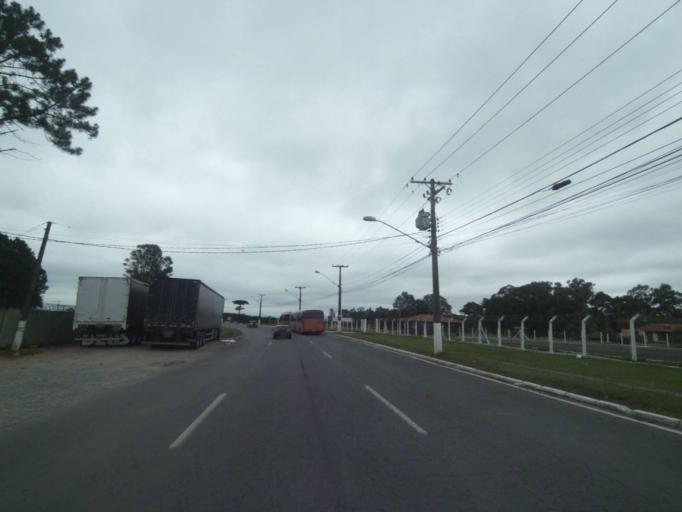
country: BR
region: Parana
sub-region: Sao Jose Dos Pinhais
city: Sao Jose dos Pinhais
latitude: -25.5393
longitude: -49.3094
